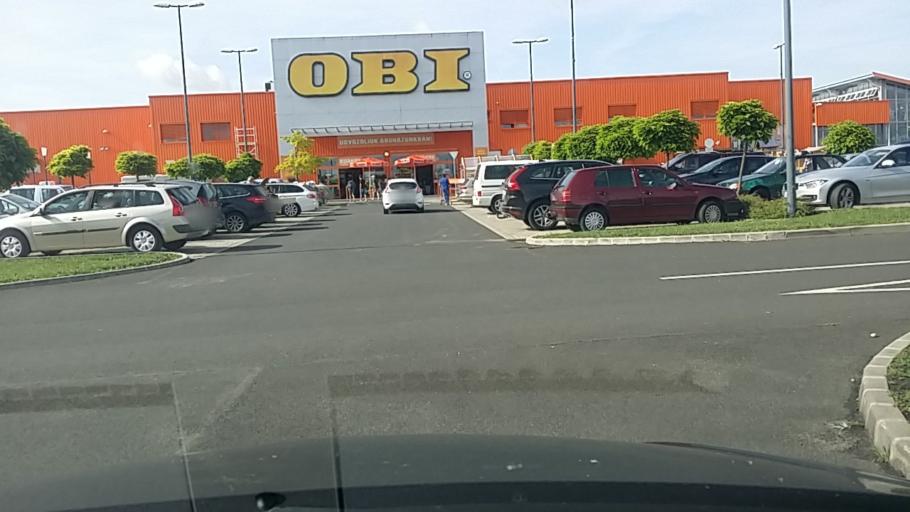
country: HU
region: Zala
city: Gyenesdias
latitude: 46.7736
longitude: 17.2648
